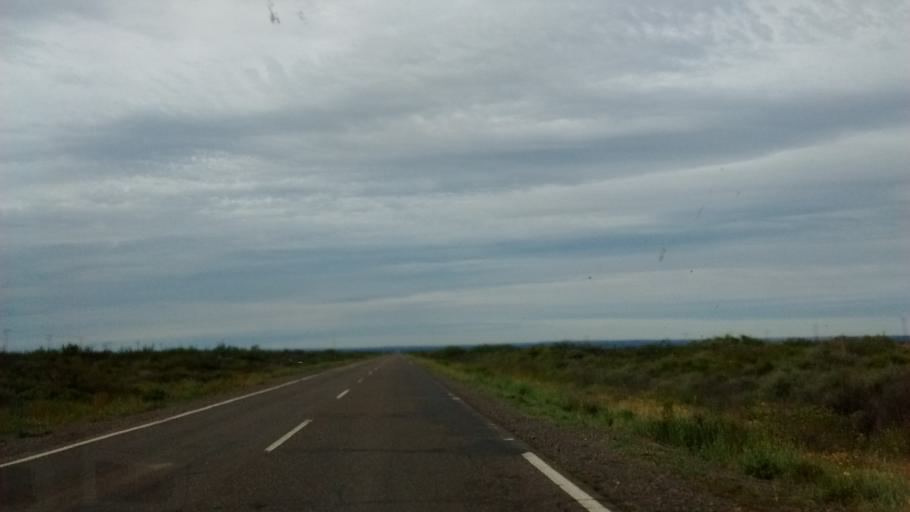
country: AR
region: Rio Negro
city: Catriel
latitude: -37.9874
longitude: -67.9093
